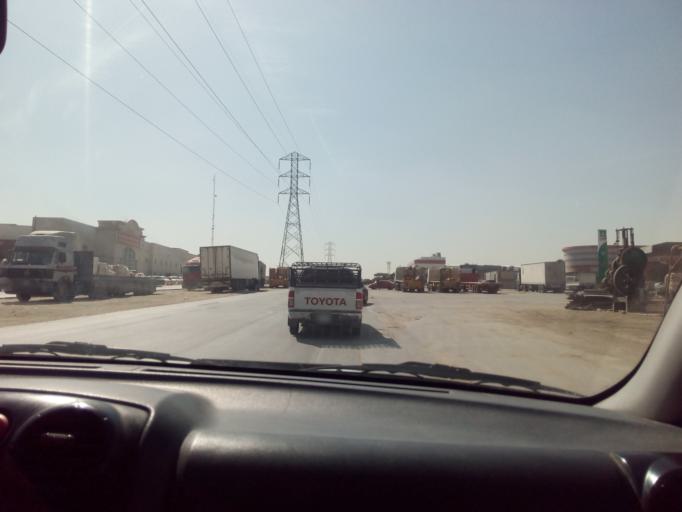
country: SA
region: Ar Riyad
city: Riyadh
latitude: 24.6651
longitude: 46.8429
